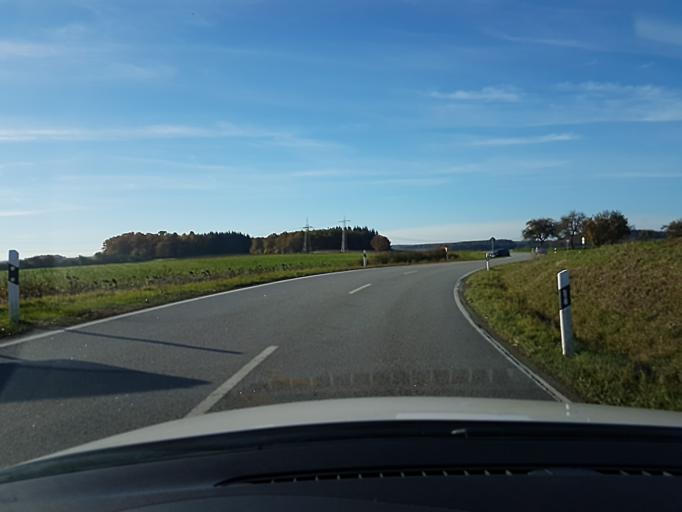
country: DE
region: Baden-Wuerttemberg
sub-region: Karlsruhe Region
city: Billigheim
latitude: 49.3482
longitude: 9.2378
